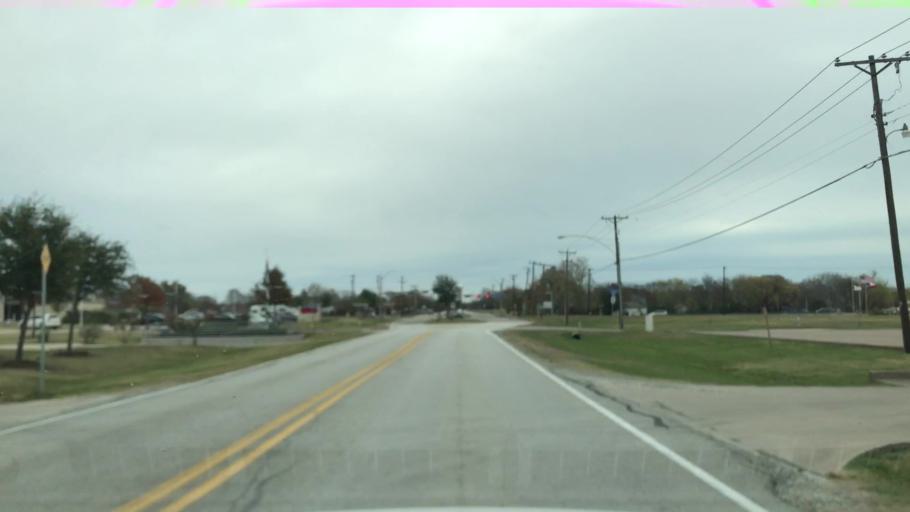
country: US
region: Texas
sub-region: Dallas County
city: Sachse
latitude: 32.9732
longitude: -96.5856
